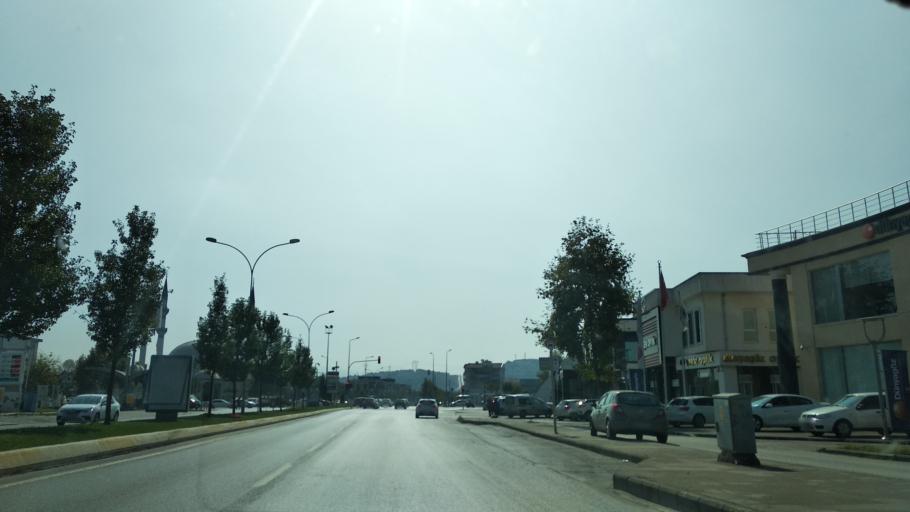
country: TR
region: Sakarya
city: Adapazari
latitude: 40.7733
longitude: 30.3640
